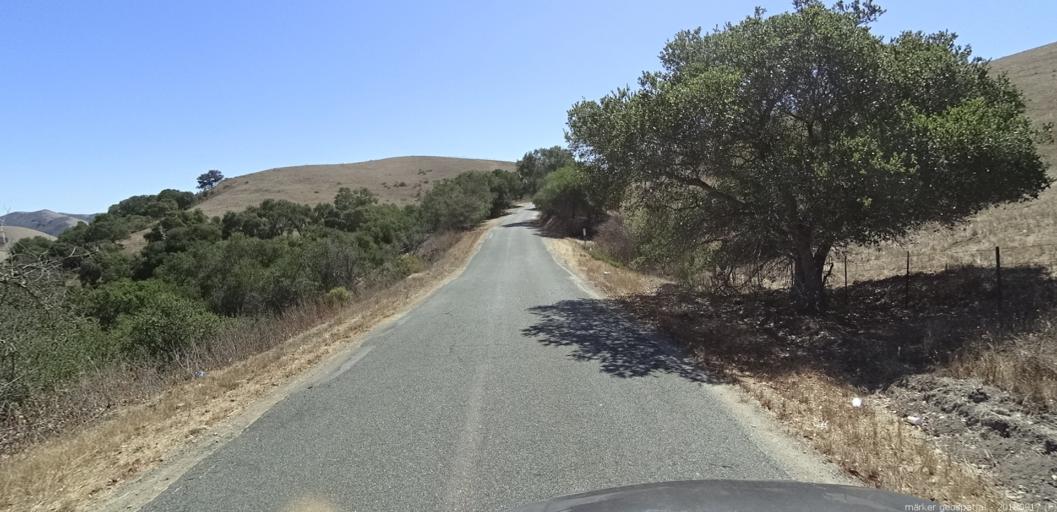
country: US
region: California
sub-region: San Benito County
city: San Juan Bautista
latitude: 36.8152
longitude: -121.5758
